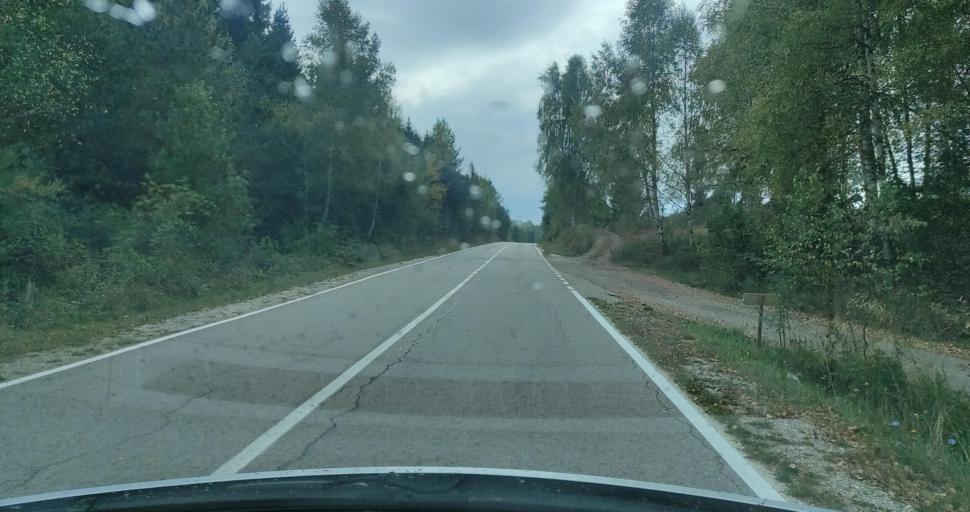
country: RS
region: Central Serbia
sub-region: Jablanicki Okrug
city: Crna Trava
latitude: 42.6891
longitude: 22.3169
